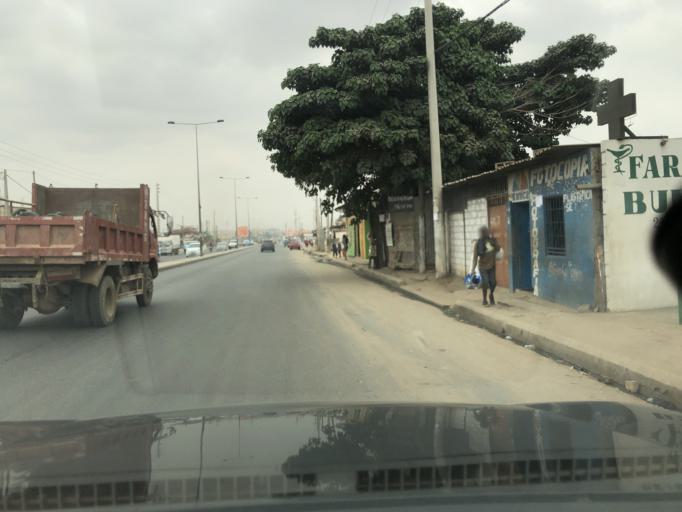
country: AO
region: Luanda
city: Luanda
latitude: -8.8319
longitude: 13.2830
